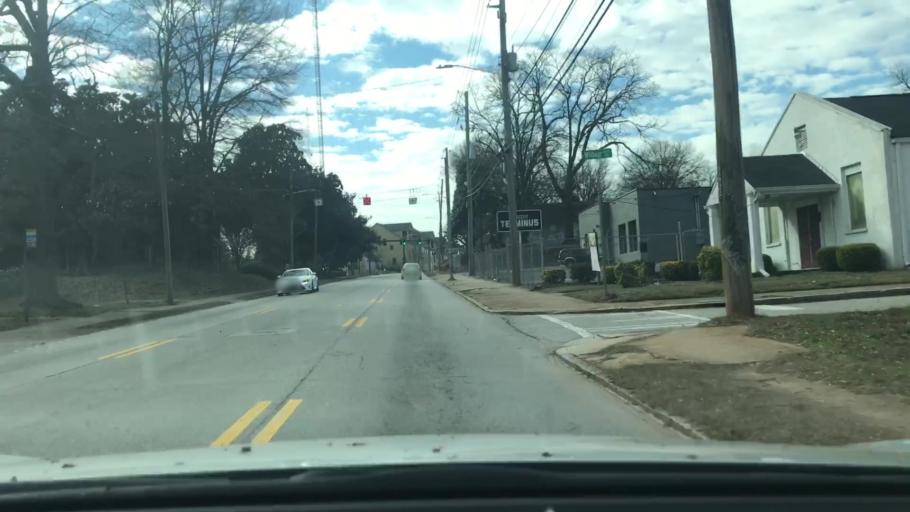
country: US
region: Georgia
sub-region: Fulton County
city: Atlanta
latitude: 33.7469
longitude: -84.3527
